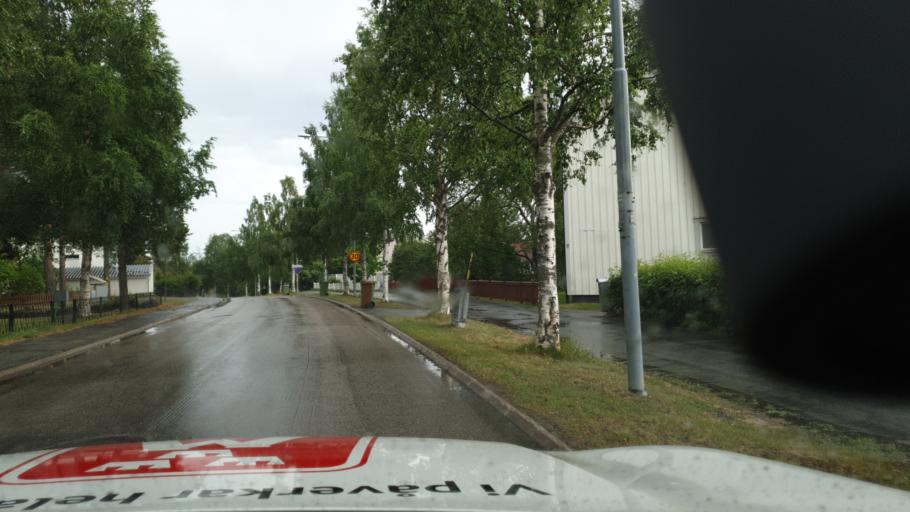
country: SE
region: Vaesterbotten
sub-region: Umea Kommun
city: Roback
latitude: 63.8376
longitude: 20.2082
